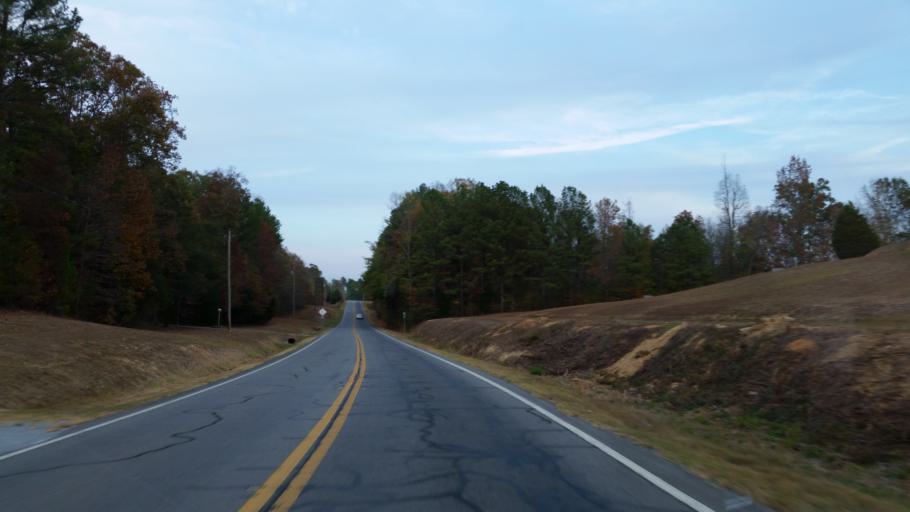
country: US
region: Georgia
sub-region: Gordon County
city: Calhoun
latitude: 34.5936
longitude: -84.8952
